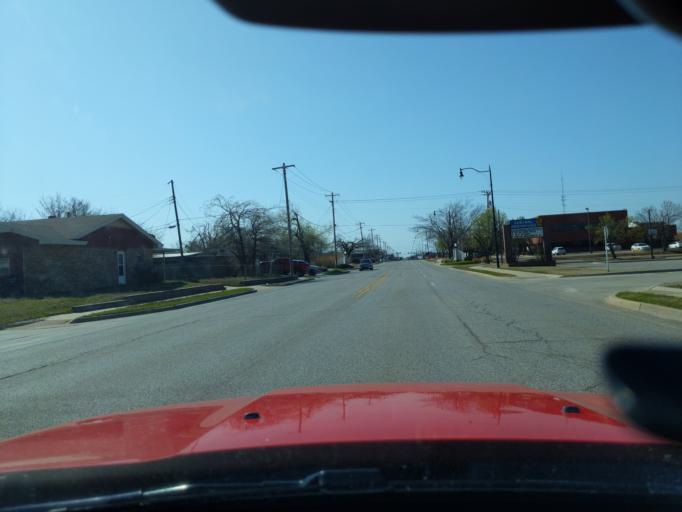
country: US
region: Oklahoma
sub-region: Cleveland County
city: Moore
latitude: 35.3424
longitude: -97.4867
